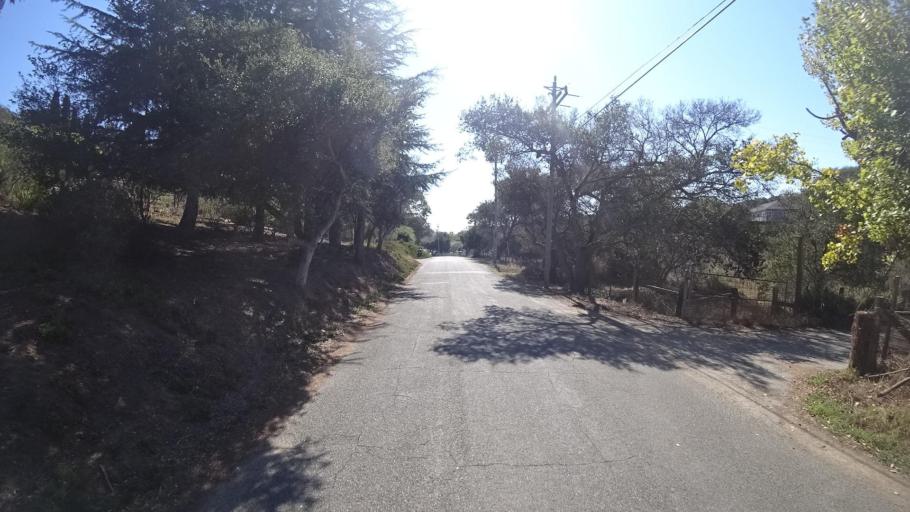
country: US
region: California
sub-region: Monterey County
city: Prunedale
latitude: 36.8185
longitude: -121.6532
